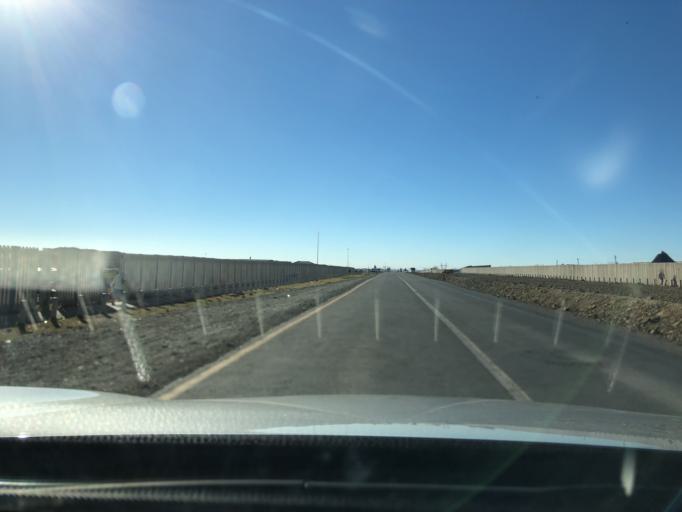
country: ZA
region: Mpumalanga
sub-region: Gert Sibande District Municipality
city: Standerton
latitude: -26.9403
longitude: 29.2046
